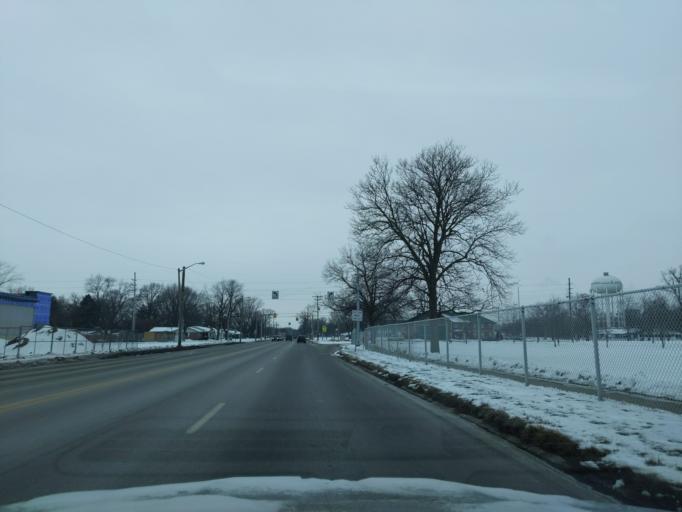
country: US
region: Indiana
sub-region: Tippecanoe County
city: Lafayette
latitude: 40.3954
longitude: -86.8747
